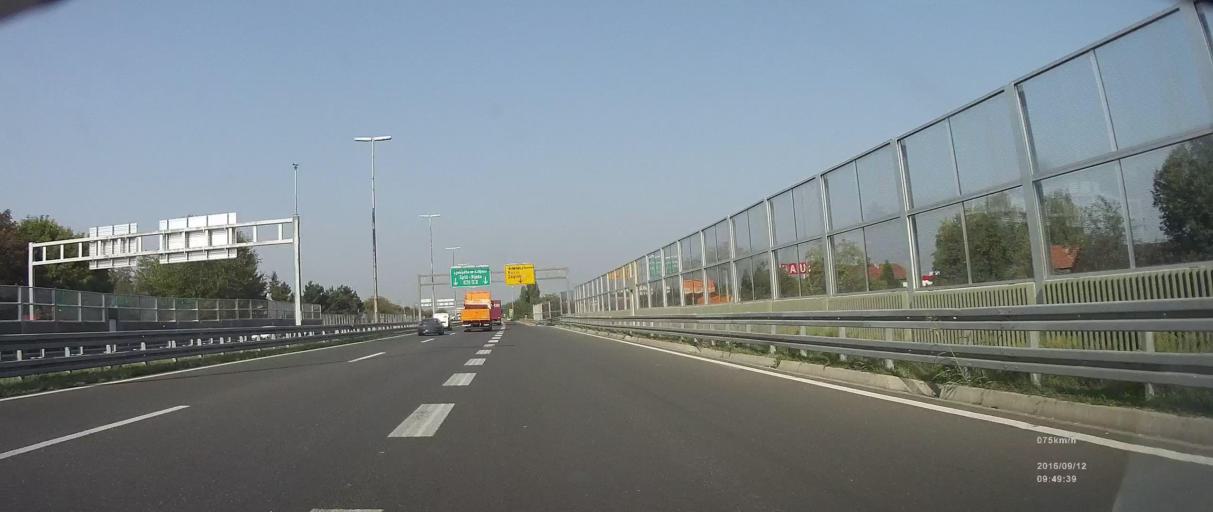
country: HR
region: Grad Zagreb
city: Odra
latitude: 45.7525
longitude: 15.9986
